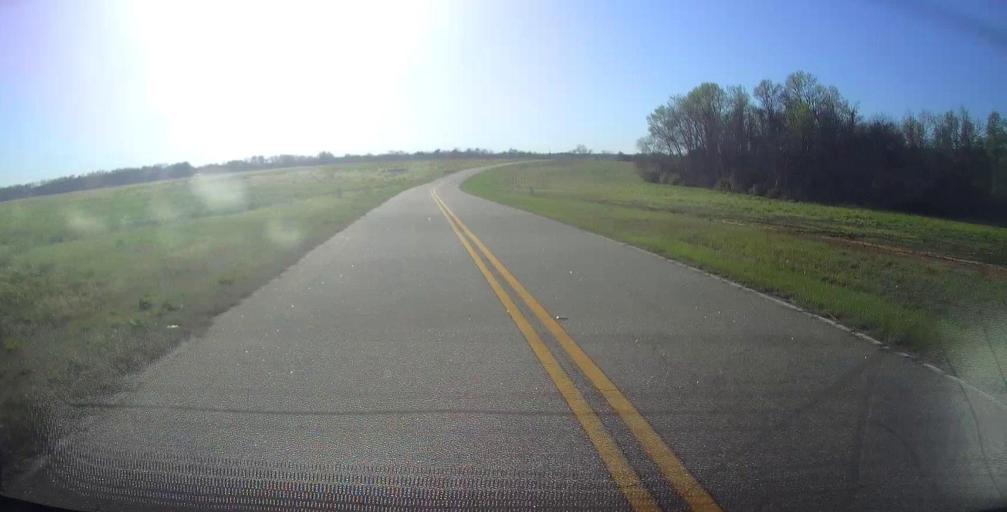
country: US
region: Georgia
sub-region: Houston County
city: Perry
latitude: 32.3676
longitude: -83.6909
